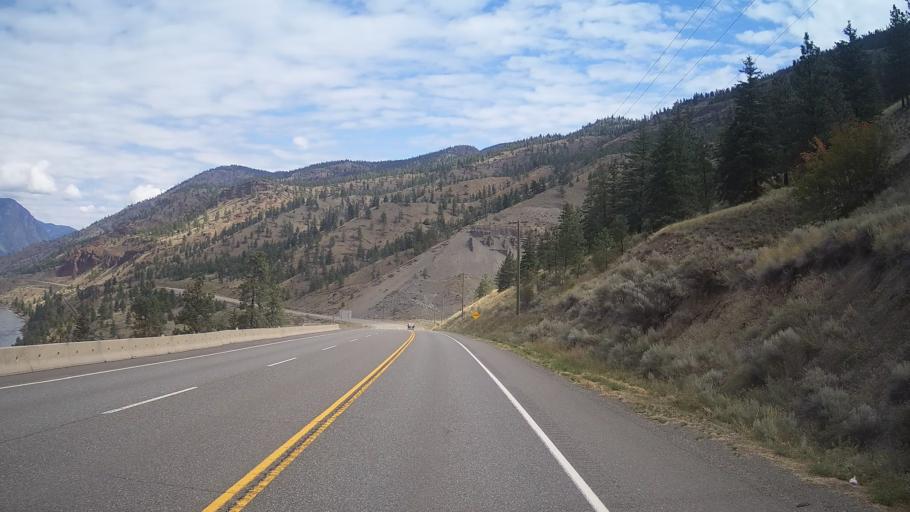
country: CA
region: British Columbia
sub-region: Thompson-Nicola Regional District
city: Ashcroft
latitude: 50.2918
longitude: -121.3954
